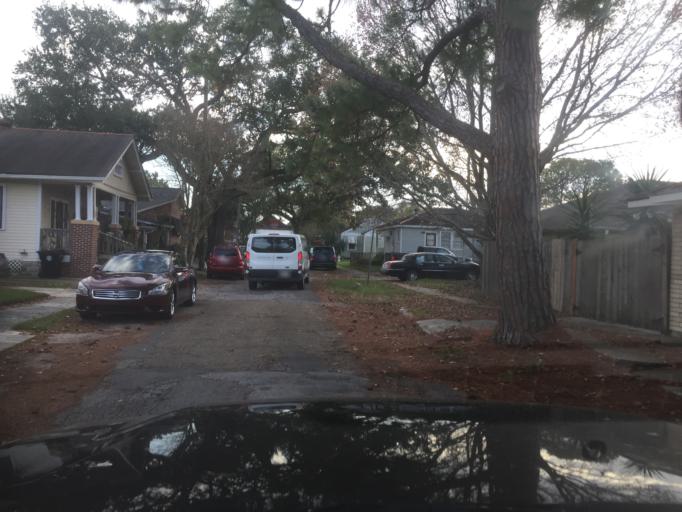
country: US
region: Louisiana
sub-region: Orleans Parish
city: New Orleans
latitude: 29.9875
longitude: -90.0786
